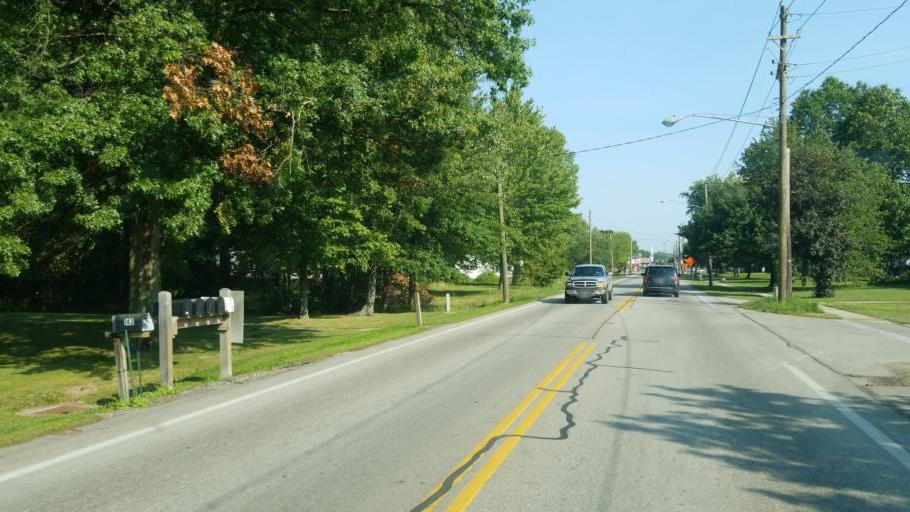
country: US
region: Ohio
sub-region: Ashtabula County
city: Orwell
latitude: 41.5313
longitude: -80.8679
